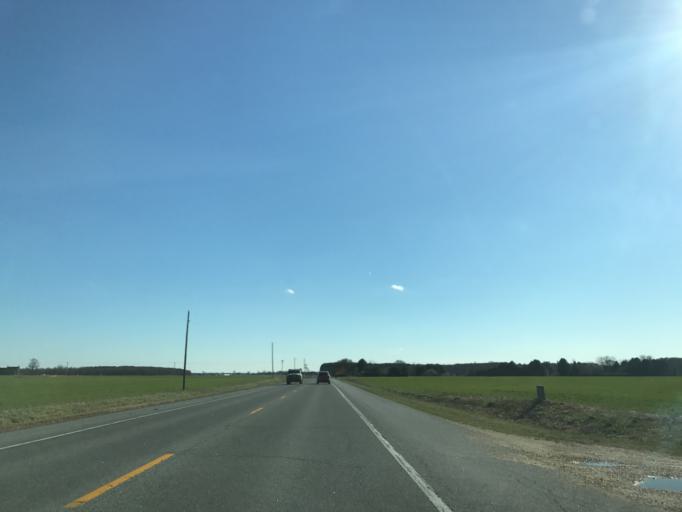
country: US
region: Maryland
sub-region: Caroline County
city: Greensboro
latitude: 39.1185
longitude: -75.8692
